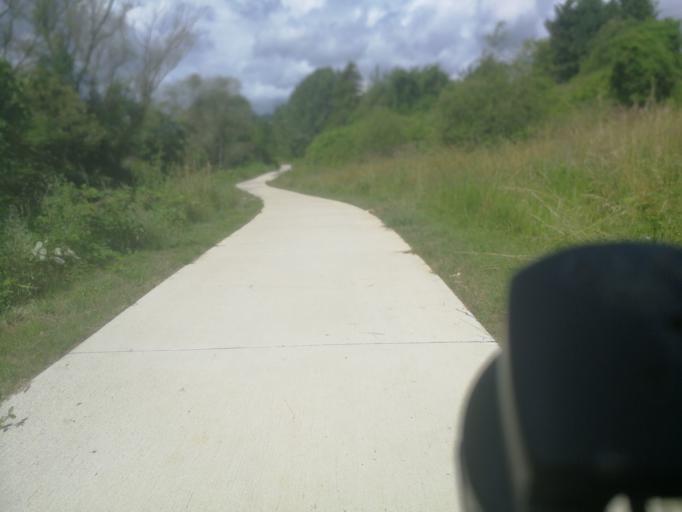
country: FR
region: Lorraine
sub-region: Departement de la Moselle
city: Vitry-sur-Orne
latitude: 49.2653
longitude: 6.1178
